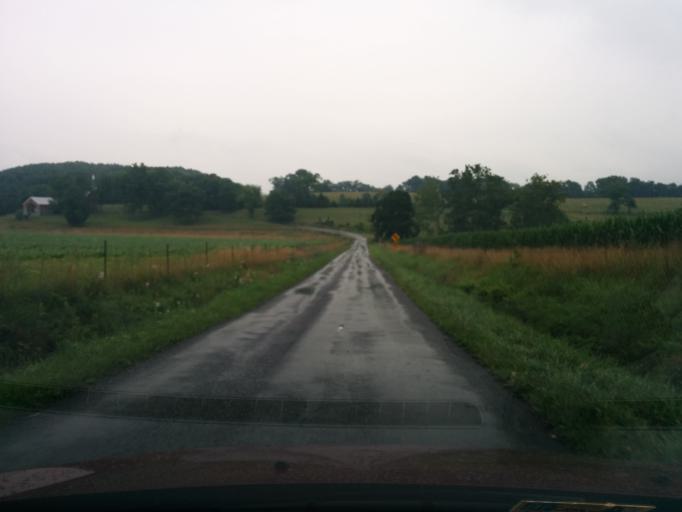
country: US
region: Virginia
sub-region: Rockbridge County
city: East Lexington
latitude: 37.8462
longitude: -79.4274
